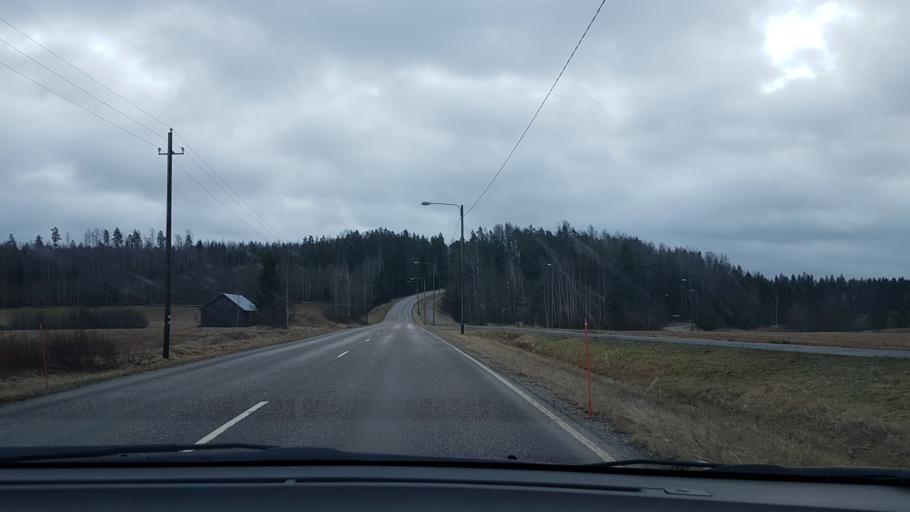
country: FI
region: Uusimaa
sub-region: Helsinki
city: Nurmijaervi
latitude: 60.4187
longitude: 24.8716
